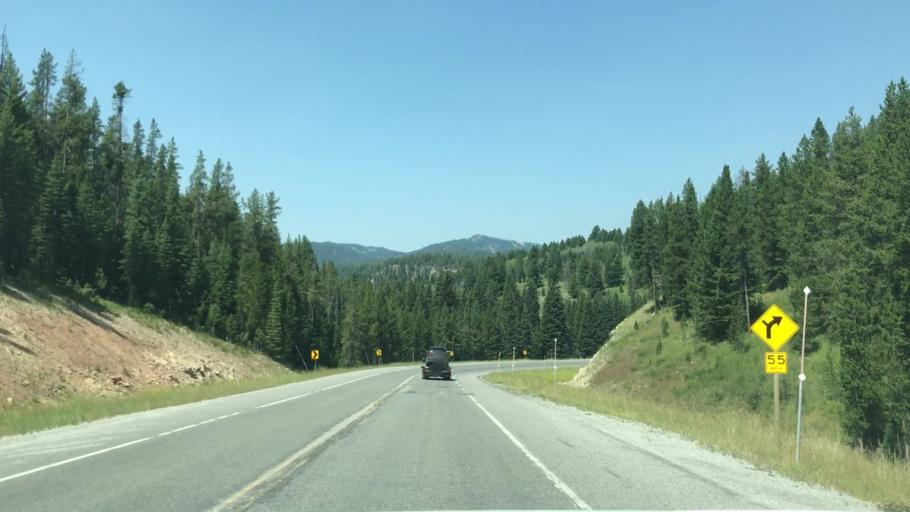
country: US
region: Montana
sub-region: Gallatin County
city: West Yellowstone
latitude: 44.8002
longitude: -111.1063
